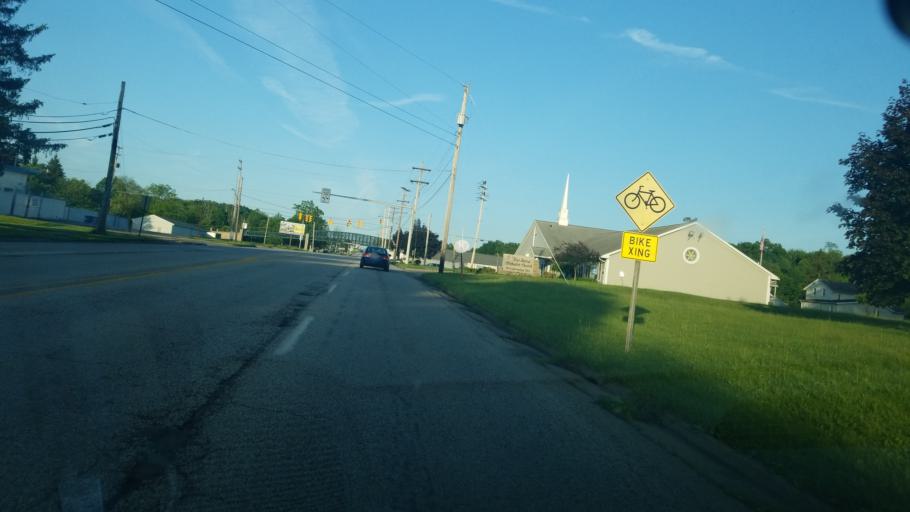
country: US
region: Ohio
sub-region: Mahoning County
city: Austintown
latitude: 41.0995
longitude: -80.7932
